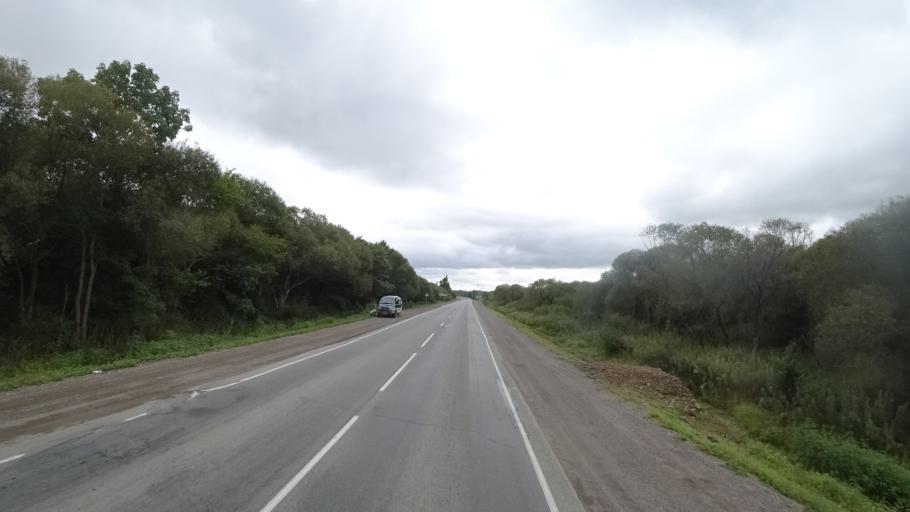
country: RU
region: Primorskiy
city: Chernigovka
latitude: 44.3445
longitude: 132.5967
